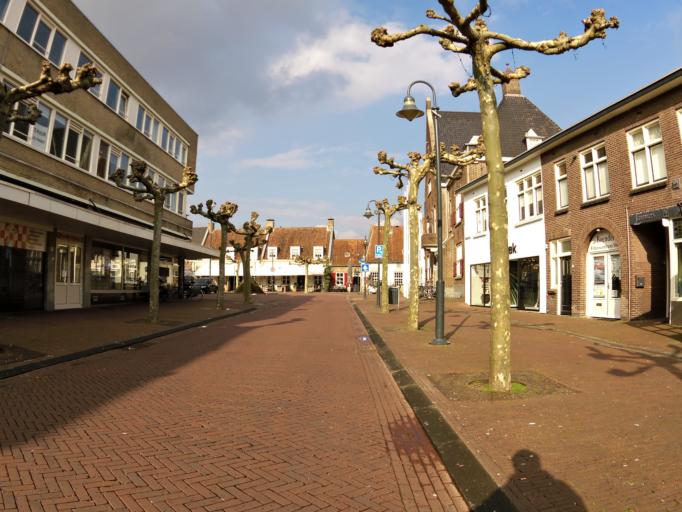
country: NL
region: North Brabant
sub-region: Gemeente Boxtel
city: Boxtel
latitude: 51.5879
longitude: 5.3273
